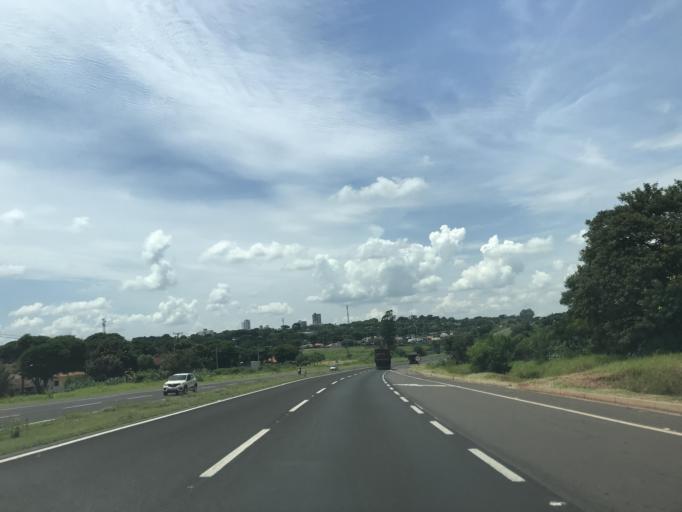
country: BR
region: Parana
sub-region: Alto Parana
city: Alto Parana
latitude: -23.1815
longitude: -52.2171
